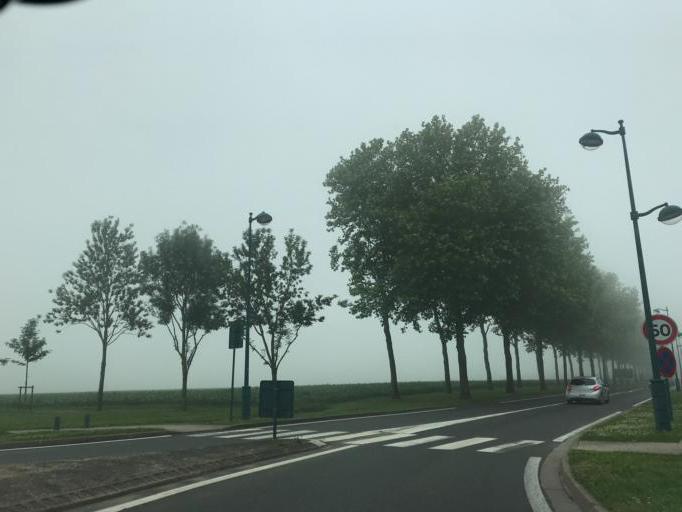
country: FR
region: Ile-de-France
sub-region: Departement de Seine-et-Marne
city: Magny-le-Hongre
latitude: 48.8744
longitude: 2.8020
